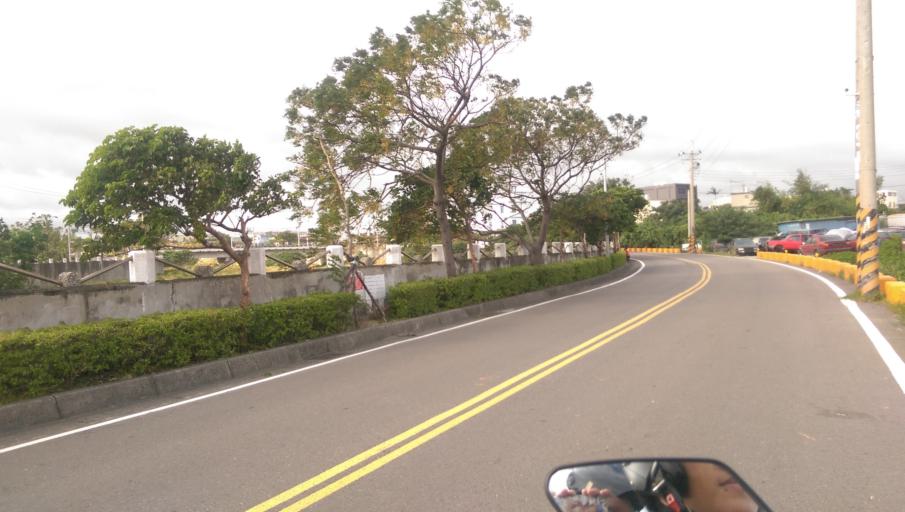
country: TW
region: Taiwan
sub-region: Hsinchu
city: Hsinchu
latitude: 24.8032
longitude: 120.9365
